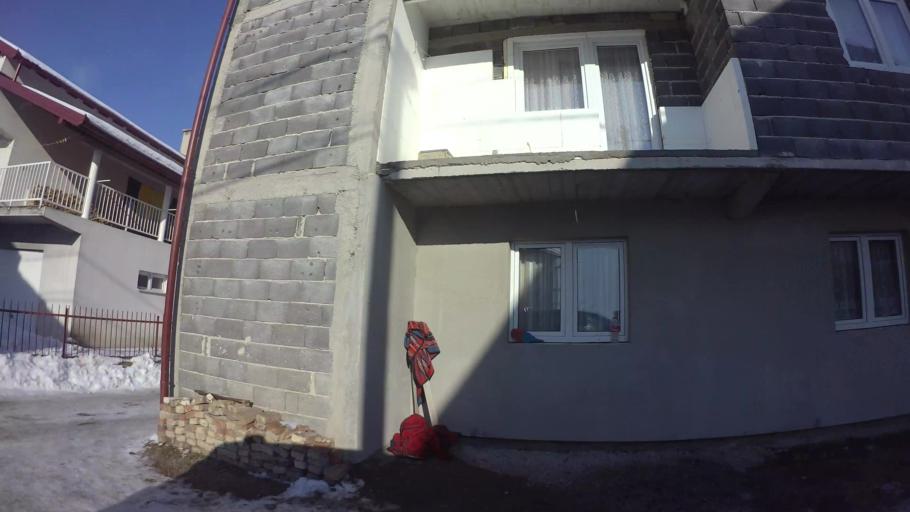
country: BA
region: Federation of Bosnia and Herzegovina
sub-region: Kanton Sarajevo
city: Sarajevo
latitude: 43.8065
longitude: 18.3310
